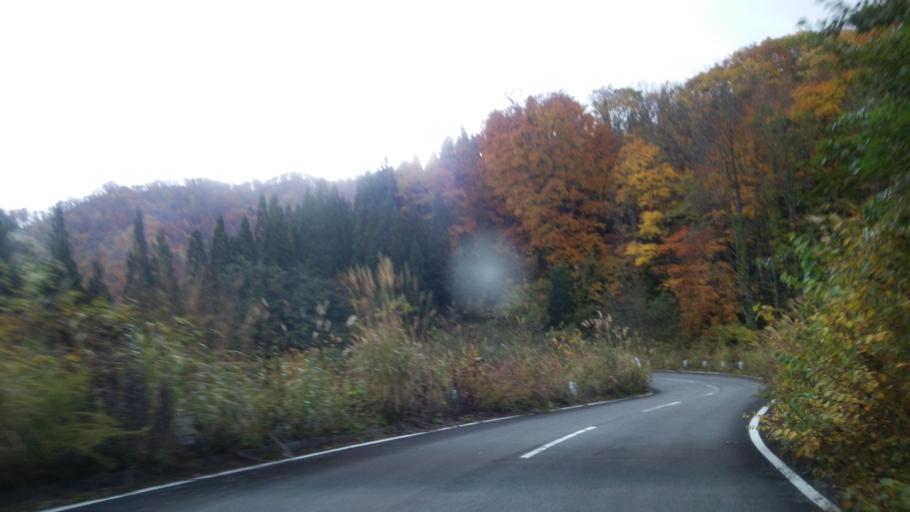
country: JP
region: Fukushima
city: Kitakata
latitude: 37.3799
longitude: 139.7248
